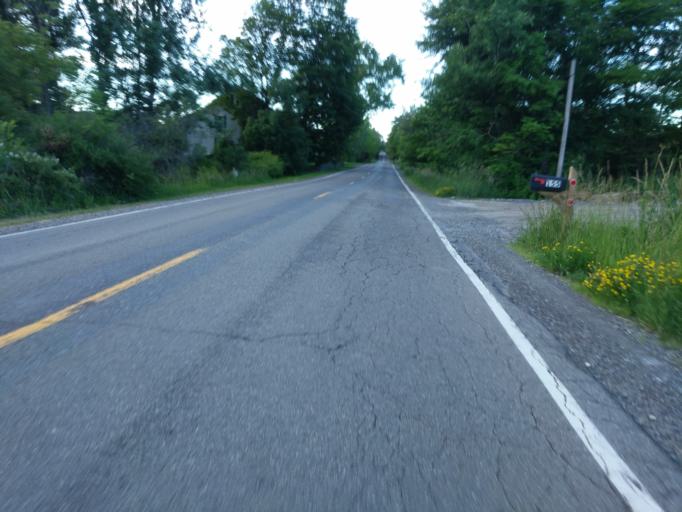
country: US
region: New York
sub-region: Tompkins County
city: Dryden
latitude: 42.4041
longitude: -76.3505
